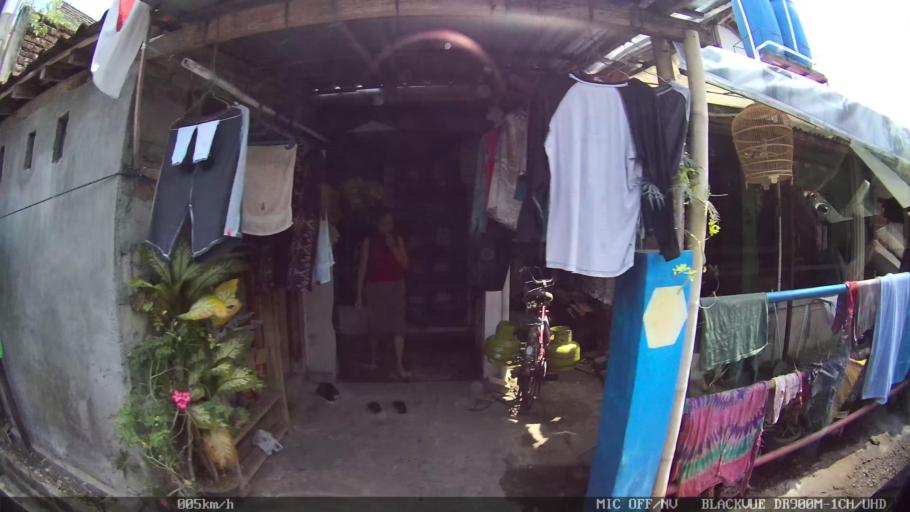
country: ID
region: Daerah Istimewa Yogyakarta
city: Yogyakarta
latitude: -7.8146
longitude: 110.3944
